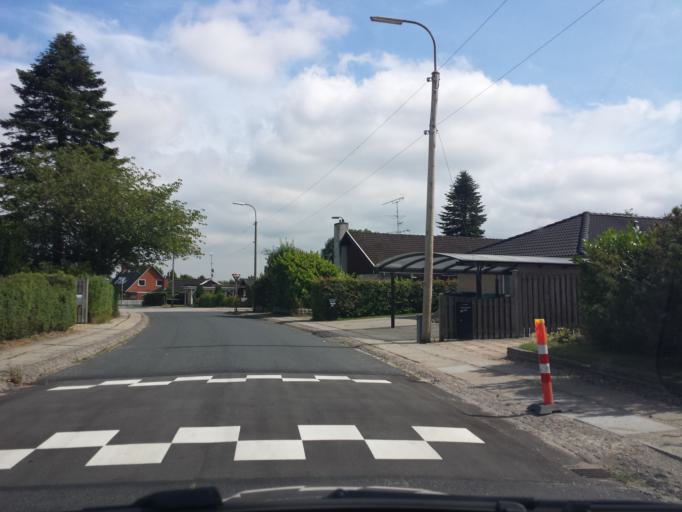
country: DK
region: Capital Region
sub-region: Ballerup Kommune
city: Ballerup
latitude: 55.7158
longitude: 12.3953
